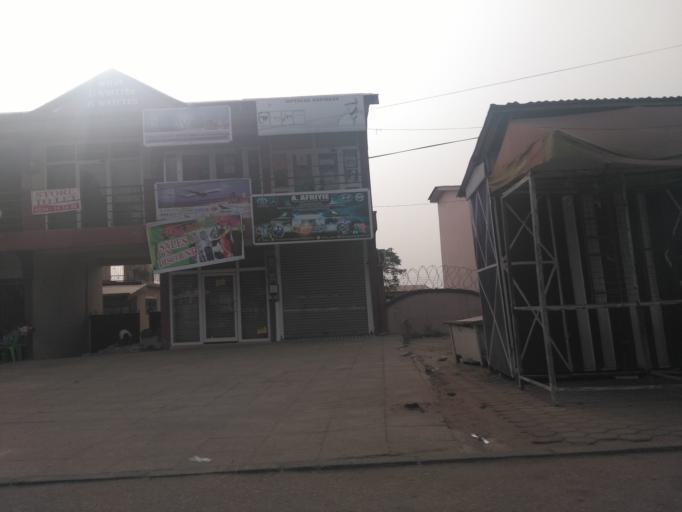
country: GH
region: Ashanti
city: Kumasi
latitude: 6.6785
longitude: -1.6439
